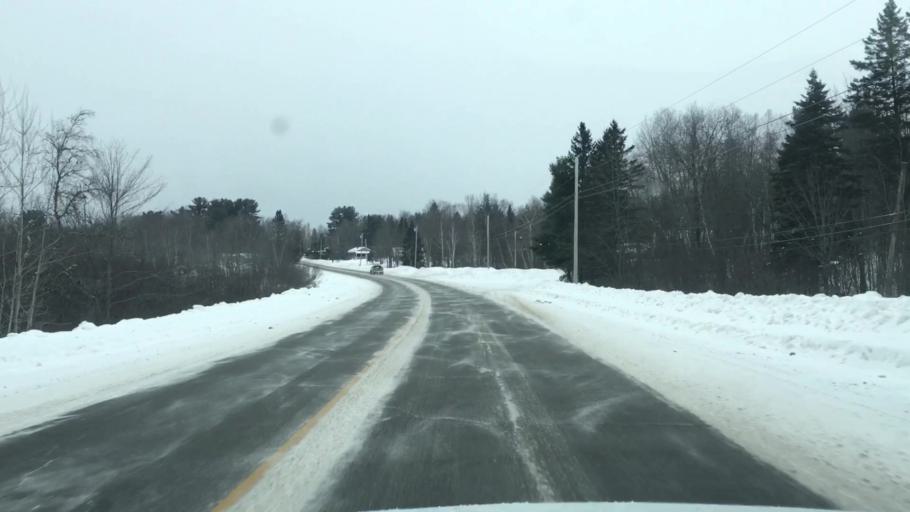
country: US
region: Maine
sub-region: Penobscot County
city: Lincoln
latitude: 45.4041
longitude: -68.4884
